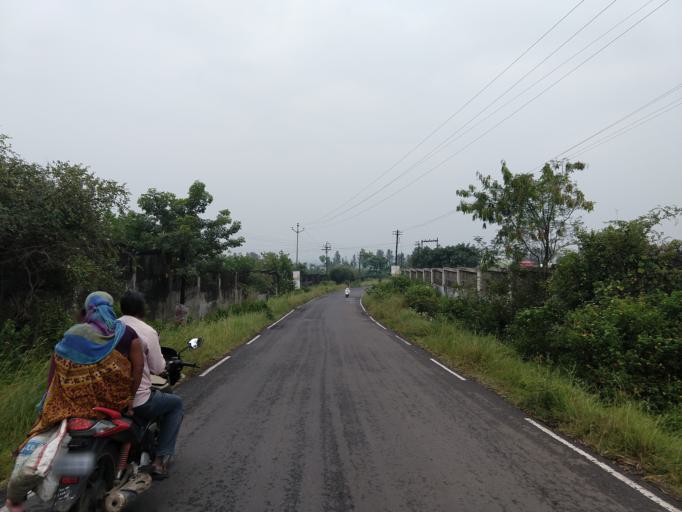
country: IN
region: Maharashtra
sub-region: Pune Division
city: Khed
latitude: 18.4042
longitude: 73.9109
